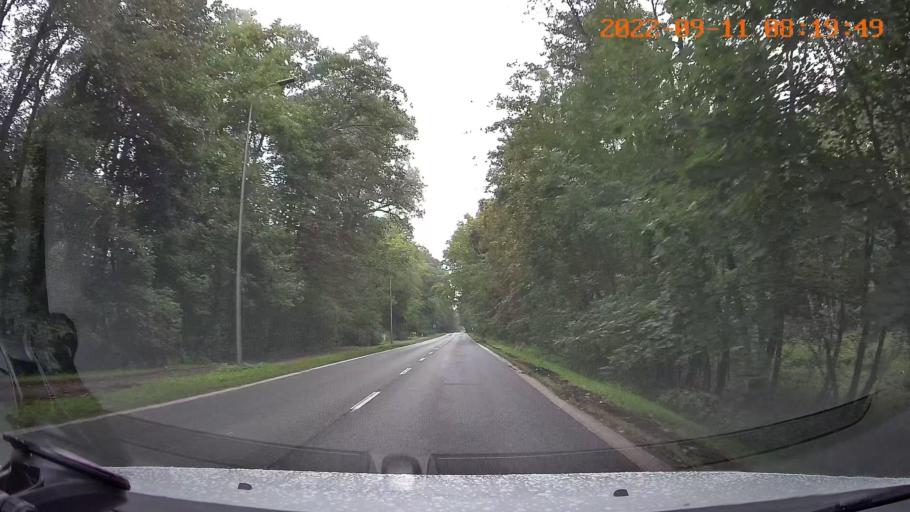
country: PL
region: Silesian Voivodeship
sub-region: Tychy
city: Tychy
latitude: 50.1542
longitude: 19.0074
